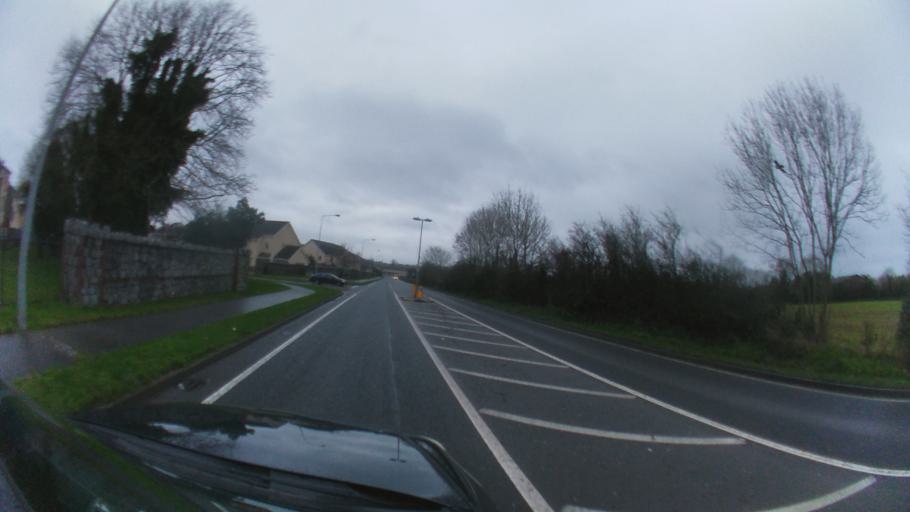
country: IE
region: Leinster
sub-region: Kildare
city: Castledermot
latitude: 52.9058
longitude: -6.8390
